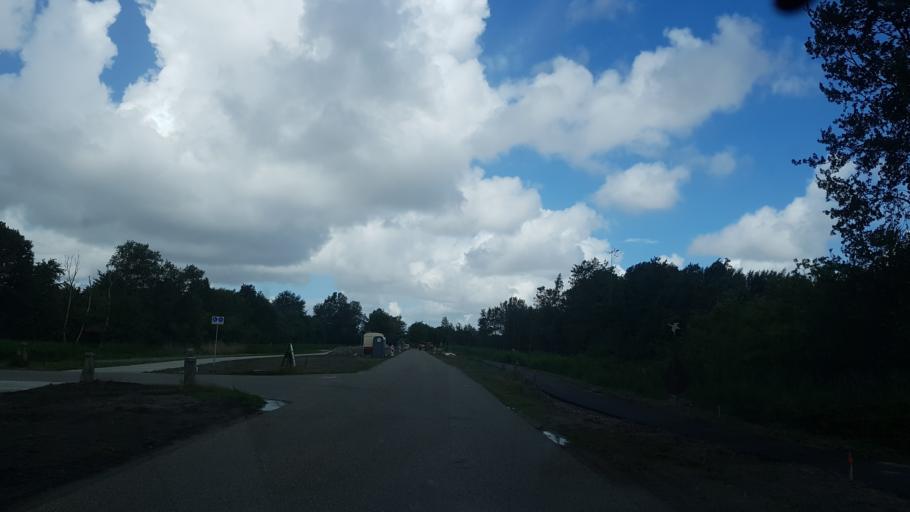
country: NL
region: Friesland
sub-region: Gemeente Dongeradeel
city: Anjum
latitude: 53.4024
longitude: 6.2181
